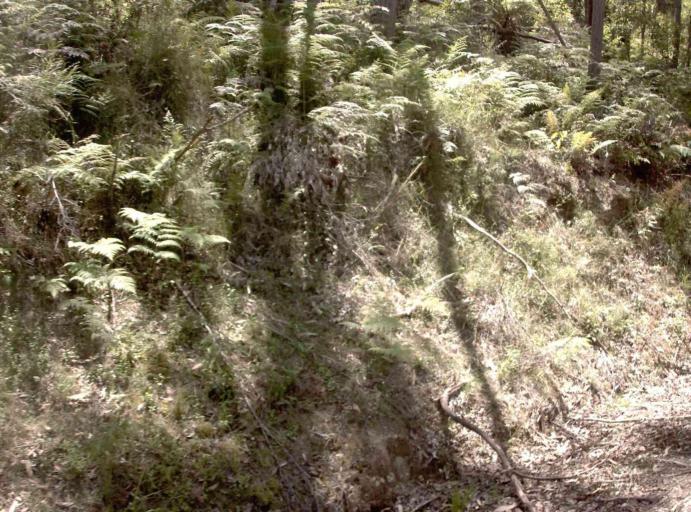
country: AU
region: New South Wales
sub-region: Bombala
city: Bombala
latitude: -37.5037
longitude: 148.9247
